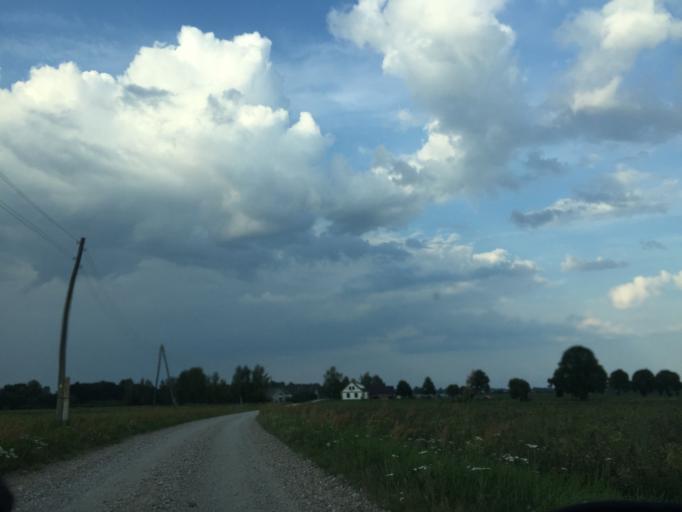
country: LV
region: Dobeles Rajons
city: Dobele
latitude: 56.6079
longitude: 23.3370
